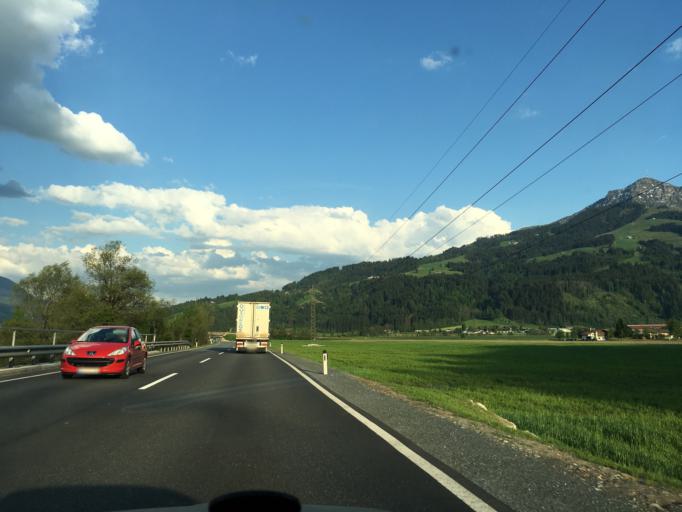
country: AT
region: Tyrol
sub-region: Politischer Bezirk Kitzbuhel
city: Oberndorf in Tirol
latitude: 47.5208
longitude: 12.3964
